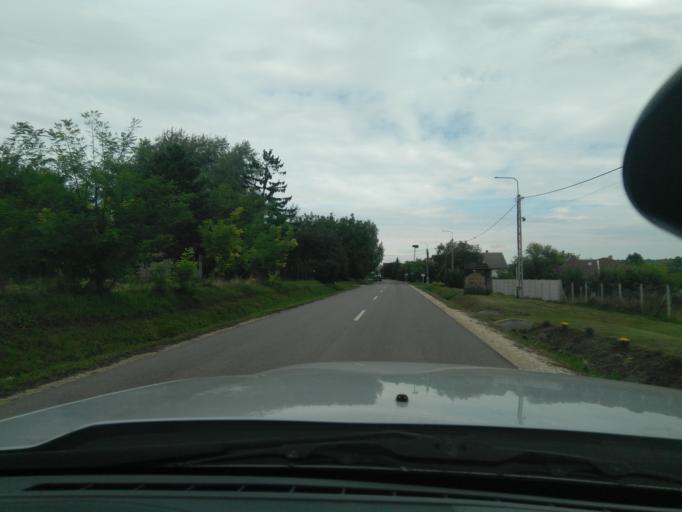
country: HU
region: Fejer
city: Val
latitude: 47.3595
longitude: 18.7359
